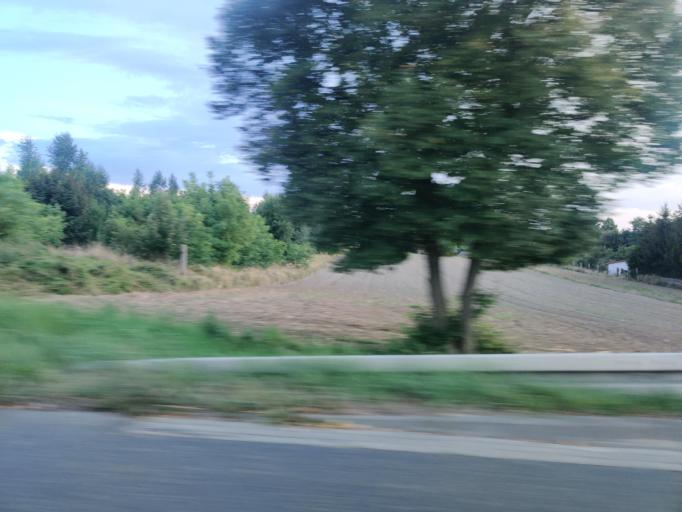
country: PL
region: Greater Poland Voivodeship
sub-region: Konin
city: Konin
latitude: 52.1957
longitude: 18.3083
